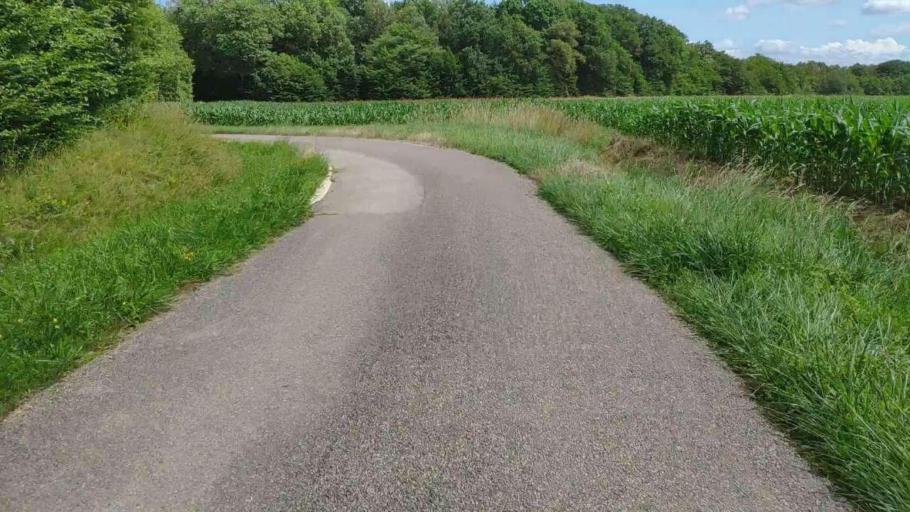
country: FR
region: Franche-Comte
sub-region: Departement du Jura
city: Chaussin
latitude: 46.9061
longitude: 5.4648
